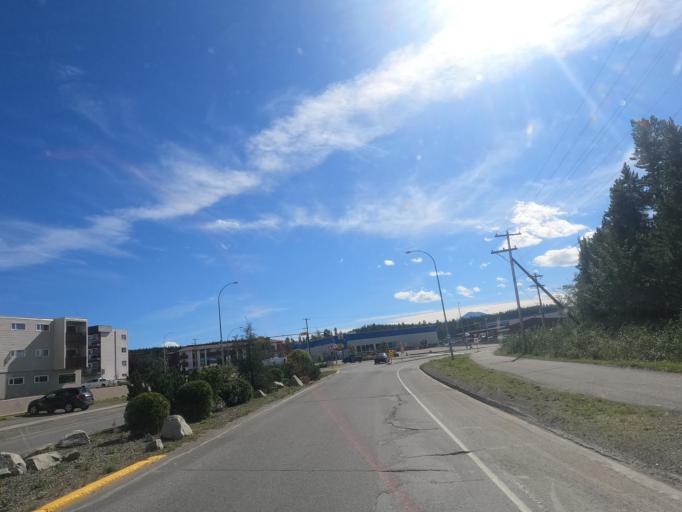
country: CA
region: Yukon
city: Whitehorse
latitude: 60.7067
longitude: -135.0346
